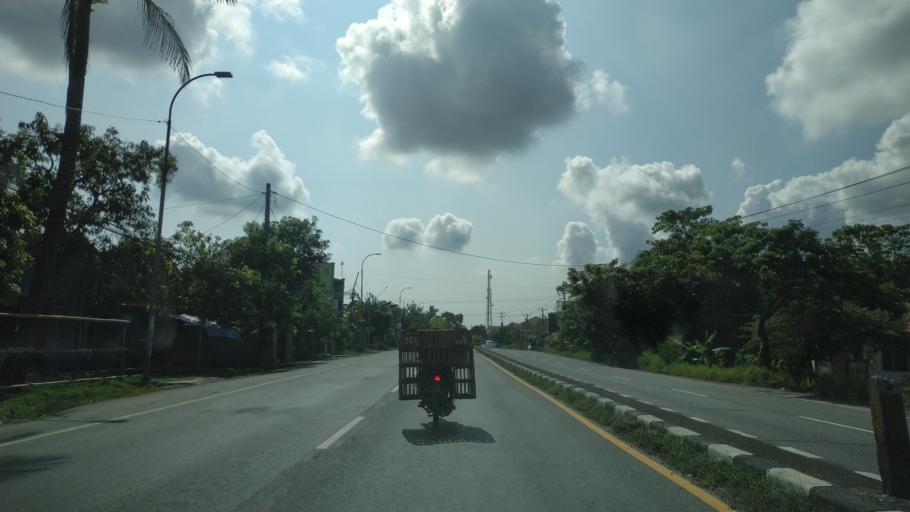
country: ID
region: Central Java
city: Comal
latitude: -6.8846
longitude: 109.5604
